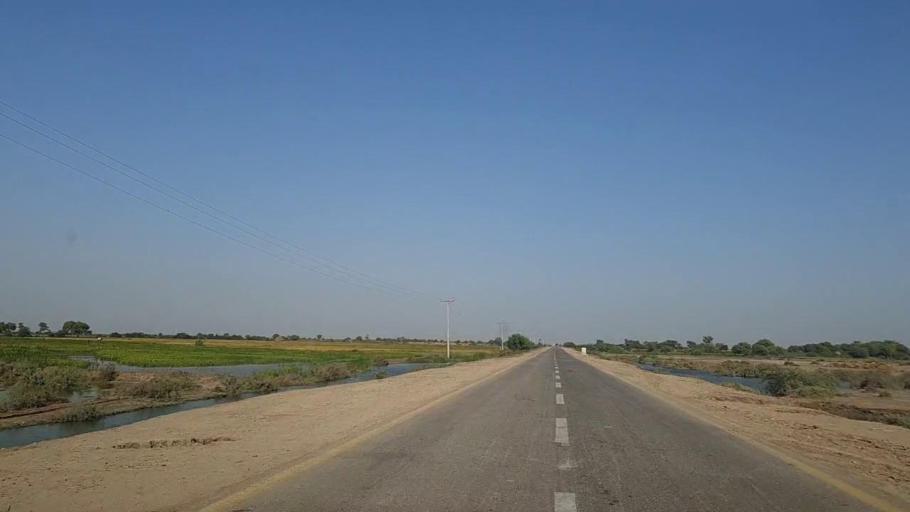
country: PK
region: Sindh
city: Jati
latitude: 24.4487
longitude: 68.3321
